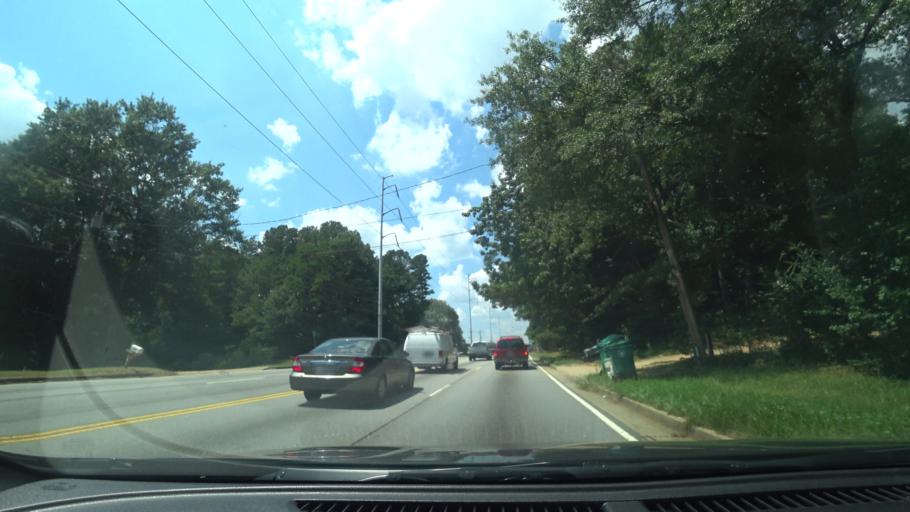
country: US
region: Georgia
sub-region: DeKalb County
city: Belvedere Park
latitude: 33.7336
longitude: -84.2095
